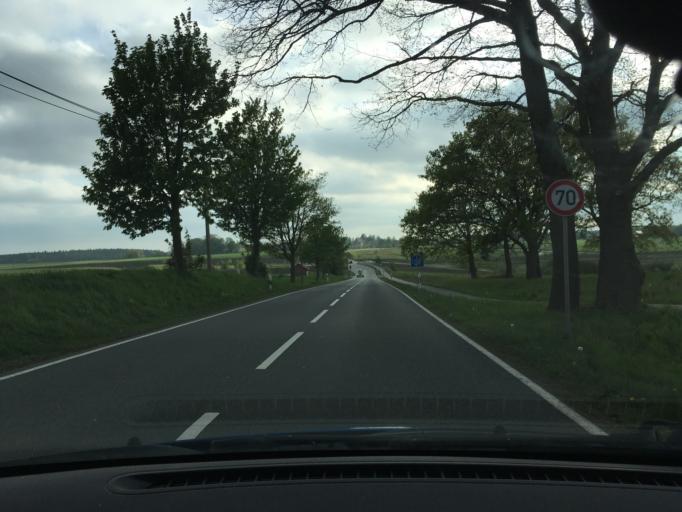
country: DE
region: Mecklenburg-Vorpommern
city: Zurow
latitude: 53.8083
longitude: 11.6122
